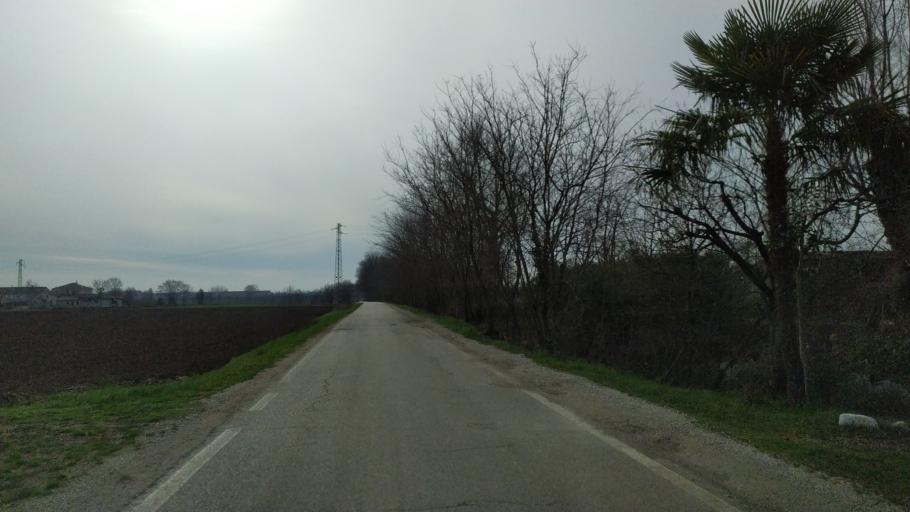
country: IT
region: Veneto
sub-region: Provincia di Vicenza
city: Isola Vicentina
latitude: 45.6550
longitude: 11.4562
